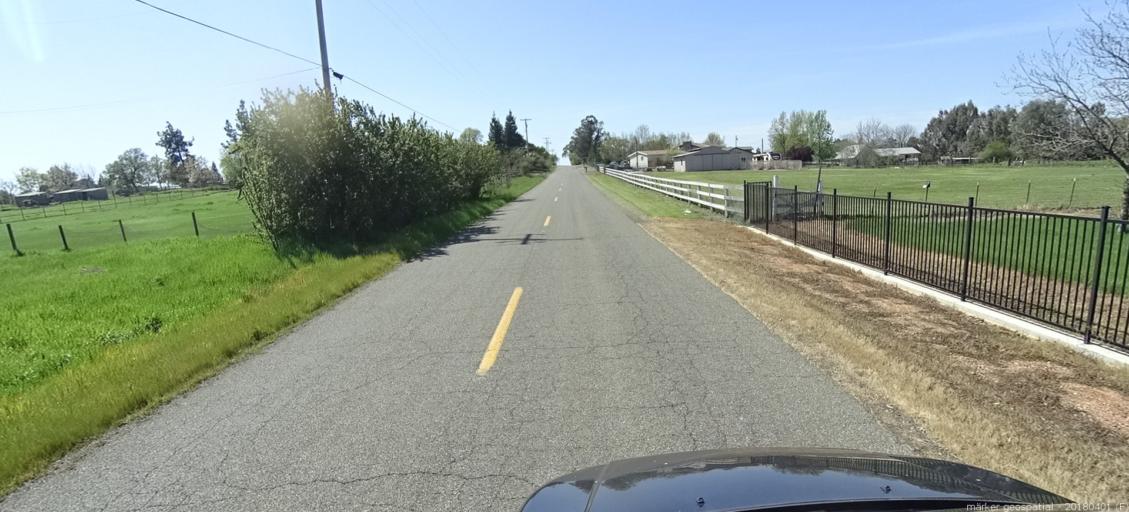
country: US
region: California
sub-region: Sacramento County
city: Wilton
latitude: 38.3941
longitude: -121.2213
